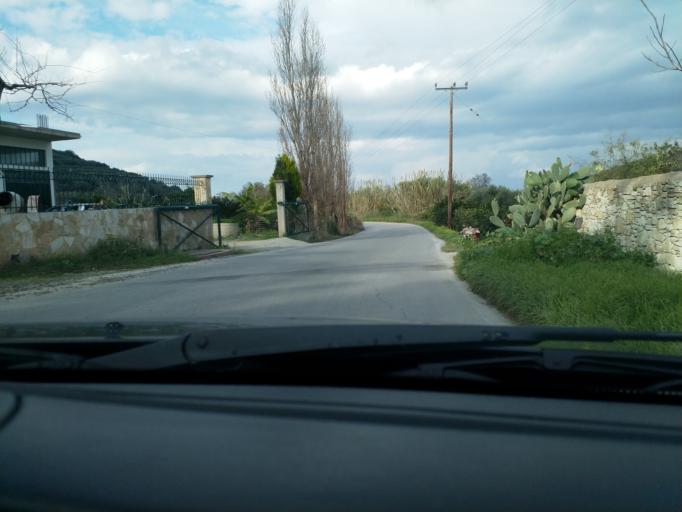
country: GR
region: Crete
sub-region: Nomos Chanias
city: Gerani
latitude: 35.5025
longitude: 23.8966
